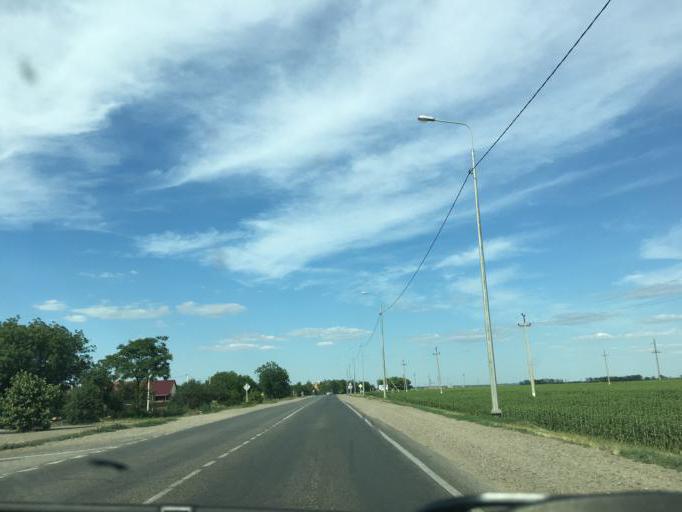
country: RU
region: Krasnodarskiy
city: Kushchevskaya
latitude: 46.5430
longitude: 39.6292
